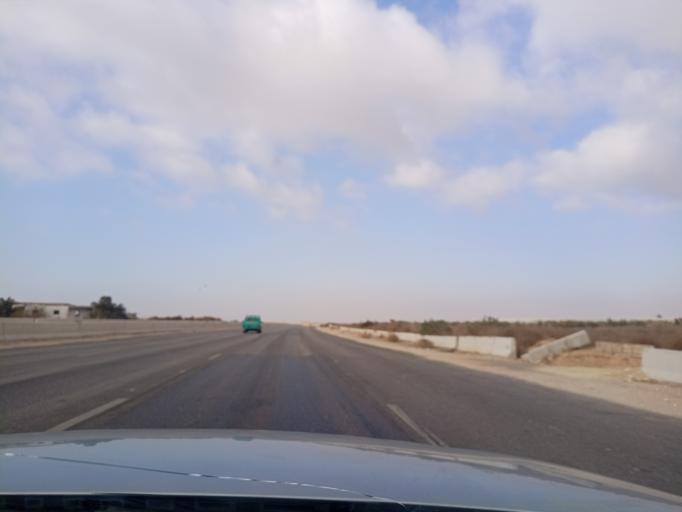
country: EG
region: Al Jizah
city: Al `Ayyat
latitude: 29.6723
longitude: 31.1982
